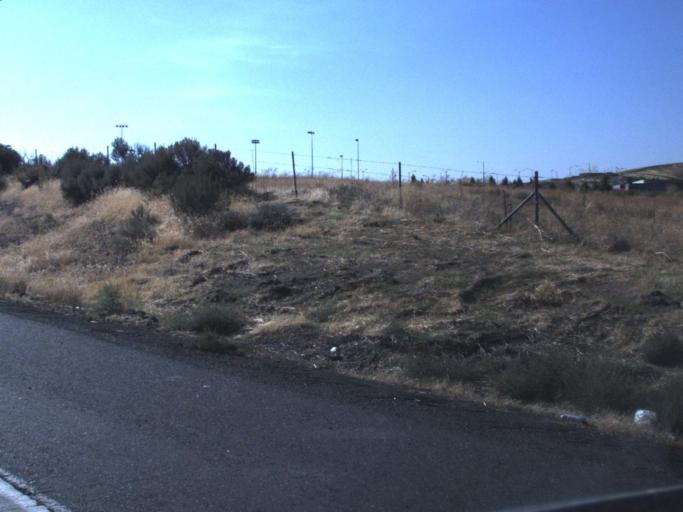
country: US
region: Washington
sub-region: Benton County
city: Kennewick
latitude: 46.1829
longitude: -119.1792
